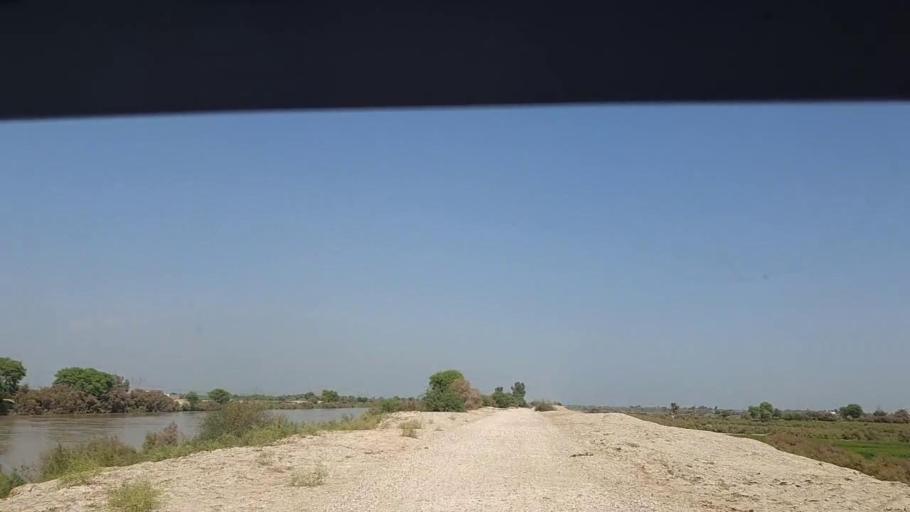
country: PK
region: Sindh
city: Kandhkot
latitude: 28.1922
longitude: 69.1656
